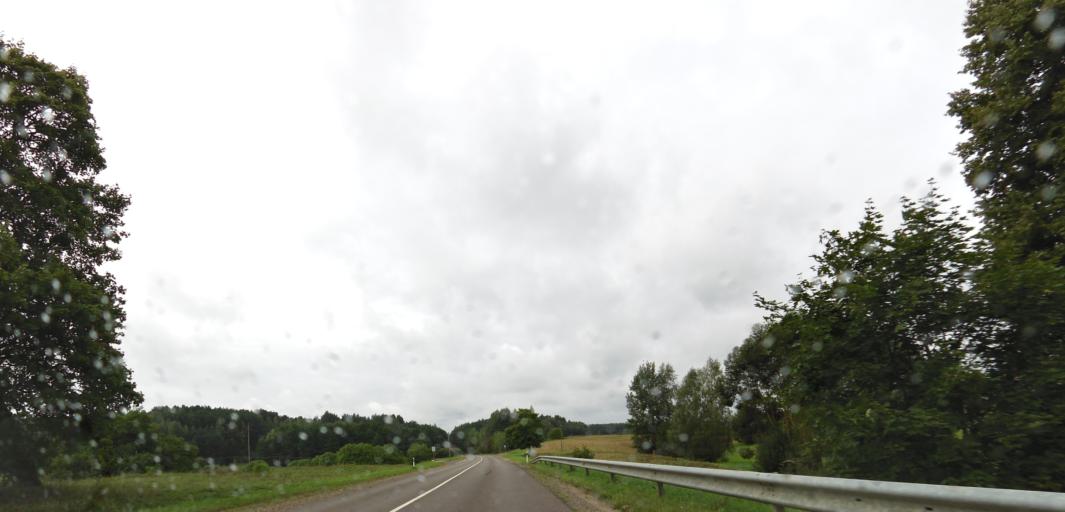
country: LT
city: Moletai
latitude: 55.2141
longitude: 25.3494
